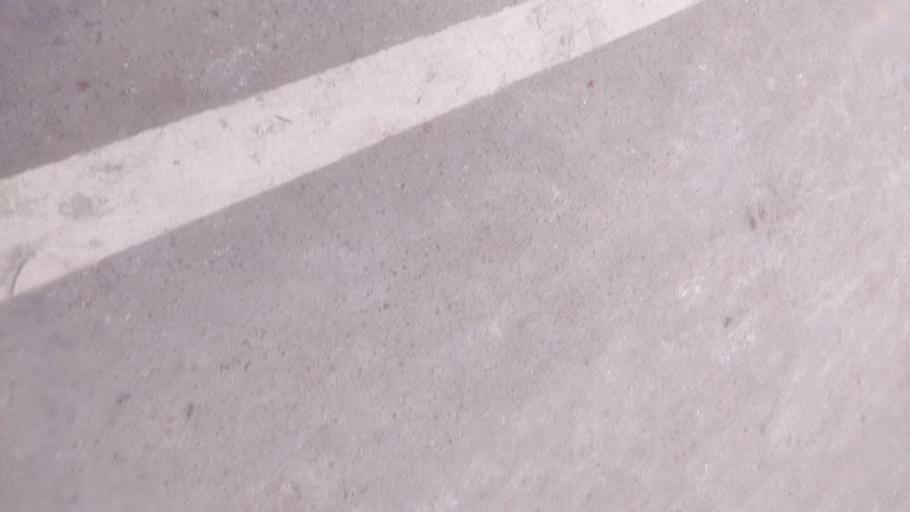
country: IN
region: Uttar Pradesh
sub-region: Faizabad
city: Ayodhya
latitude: 26.7948
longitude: 82.2023
